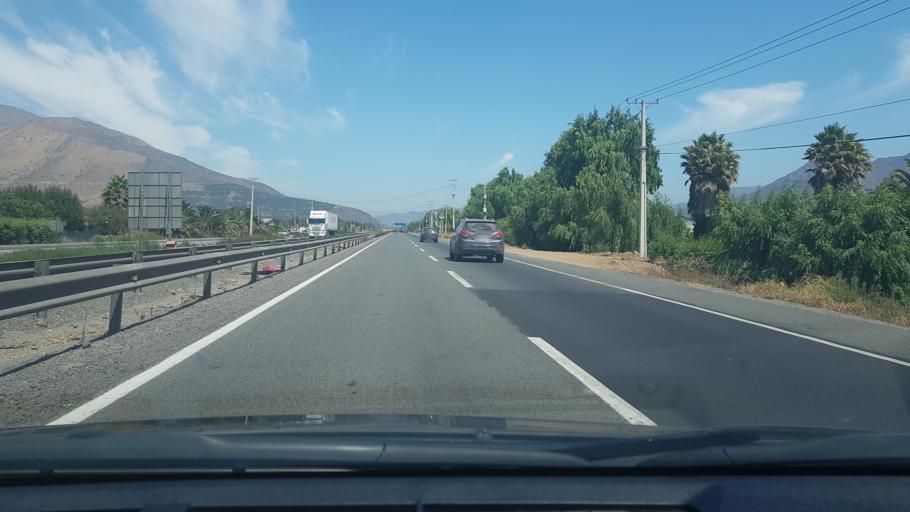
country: CL
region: Valparaiso
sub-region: Provincia de San Felipe
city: Llaillay
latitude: -32.8475
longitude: -70.9652
